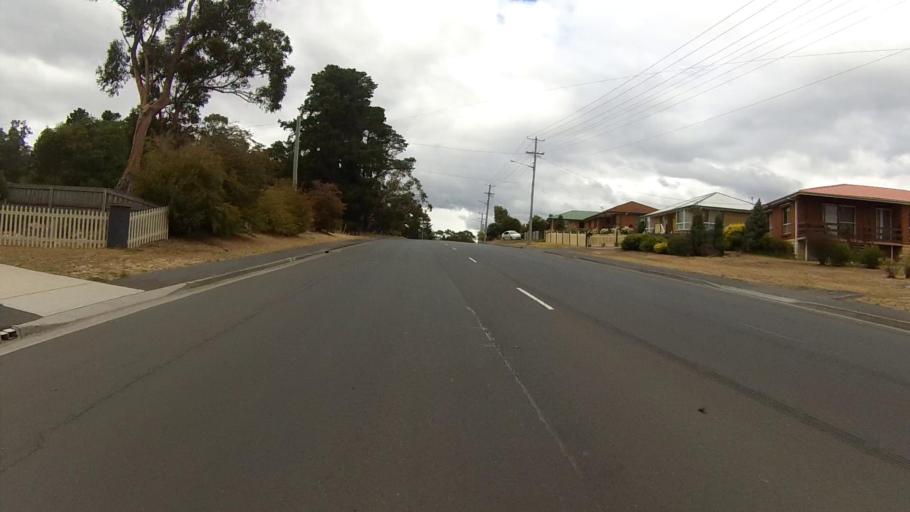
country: AU
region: Tasmania
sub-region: Glenorchy
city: Austins Ferry
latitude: -42.7694
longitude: 147.2459
